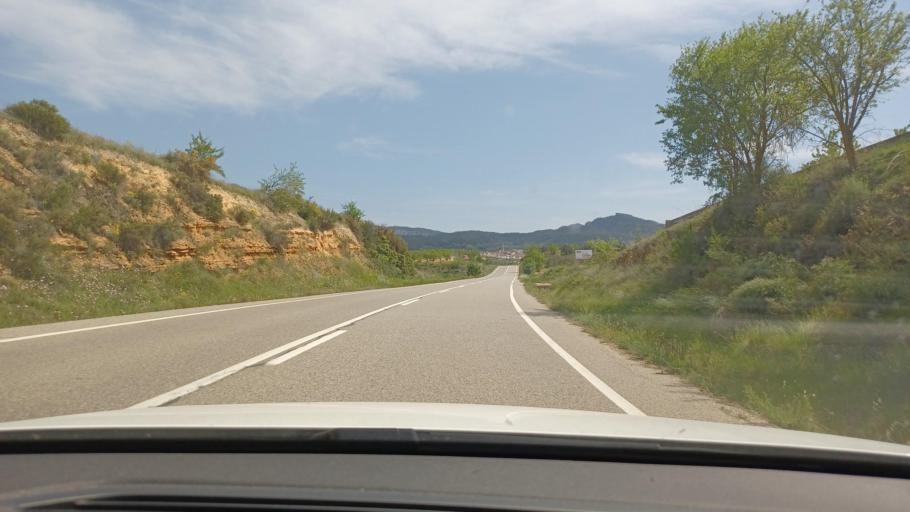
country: ES
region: Catalonia
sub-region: Provincia de Tarragona
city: Gandesa
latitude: 41.0676
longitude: 0.4318
